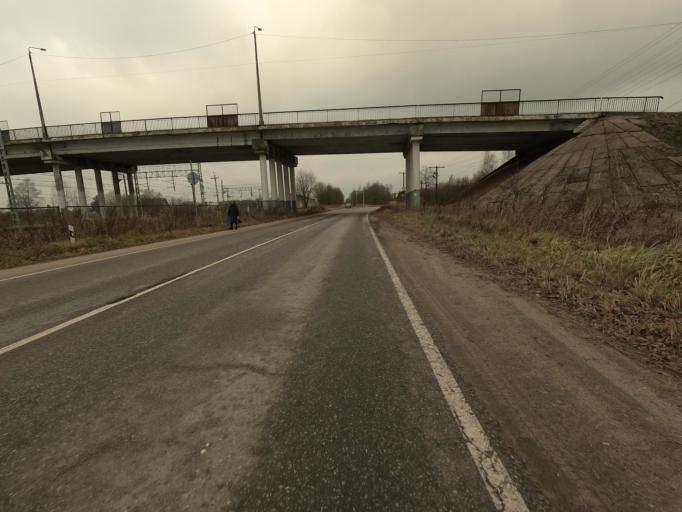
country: RU
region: Leningrad
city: Lyuban'
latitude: 59.4882
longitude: 31.2675
